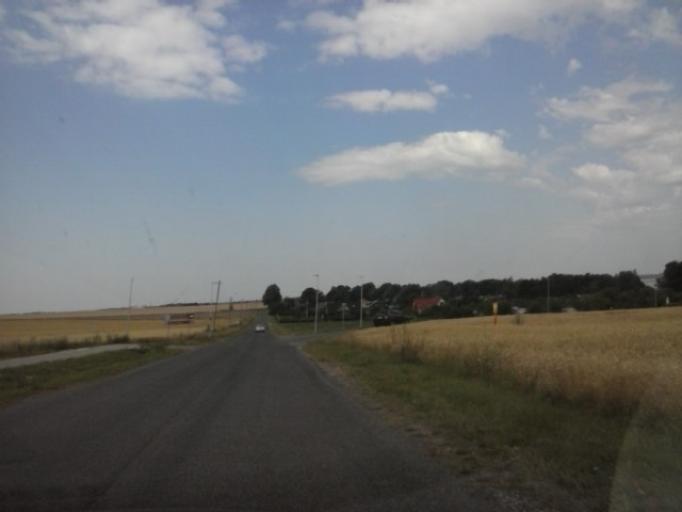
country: EE
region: Jogevamaa
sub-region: Tabivere vald
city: Tabivere
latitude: 58.5210
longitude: 26.6815
